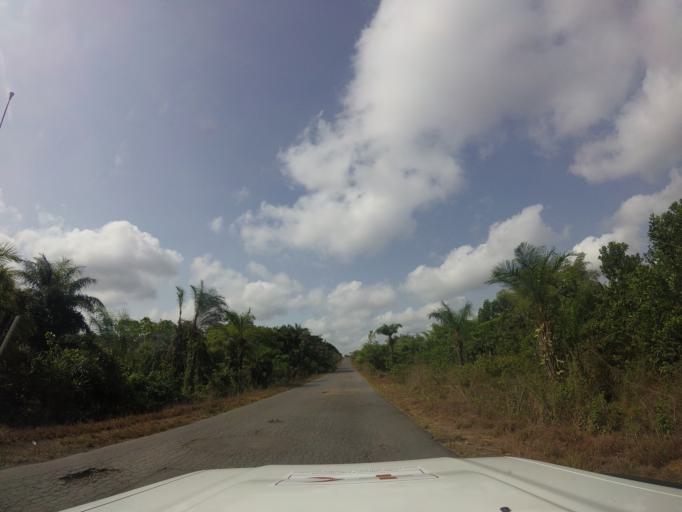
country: LR
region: Bomi
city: Tubmanburg
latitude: 6.7070
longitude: -10.8716
